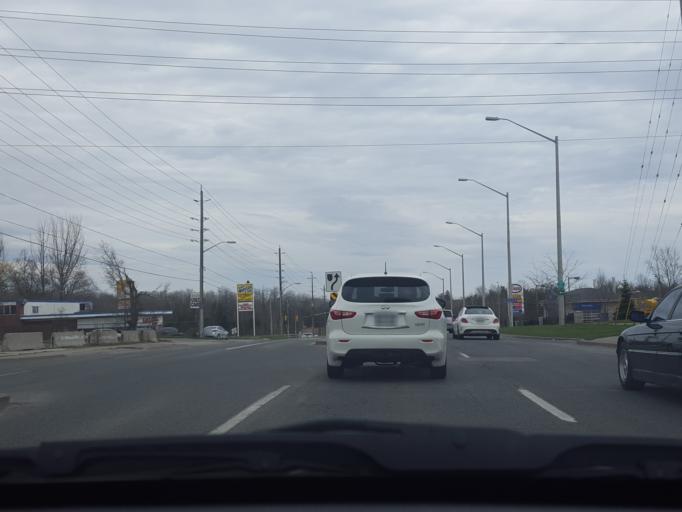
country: CA
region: Ontario
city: Ajax
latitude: 43.8461
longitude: -79.0087
